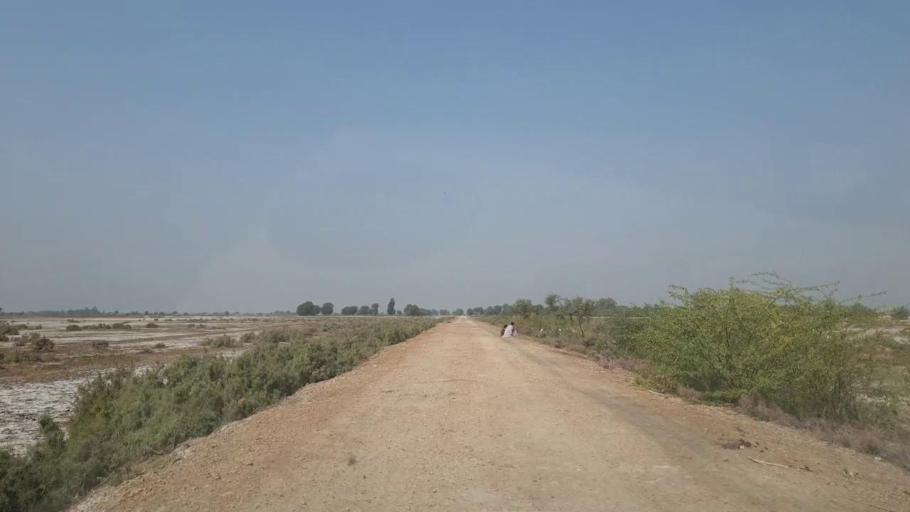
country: PK
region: Sindh
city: Mirpur Khas
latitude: 25.6523
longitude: 69.1380
